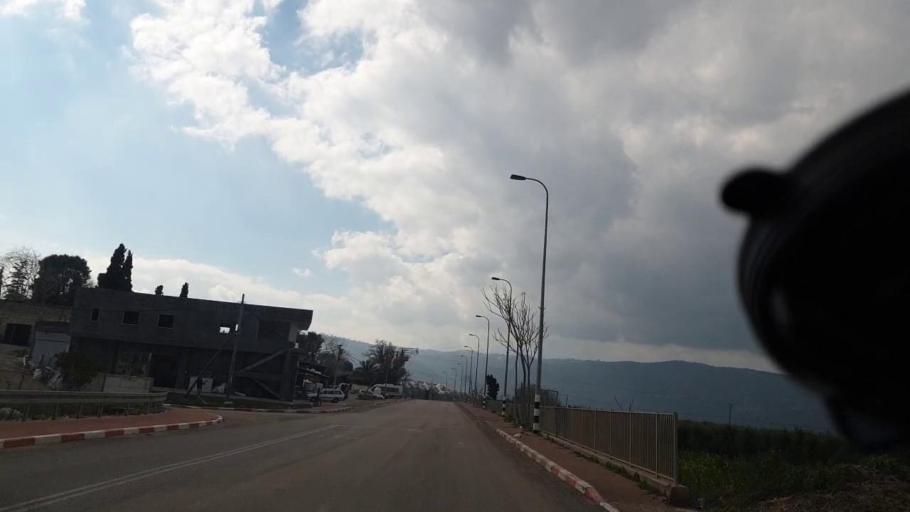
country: IL
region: Haifa
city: Ibtin
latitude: 32.7657
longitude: 35.1076
